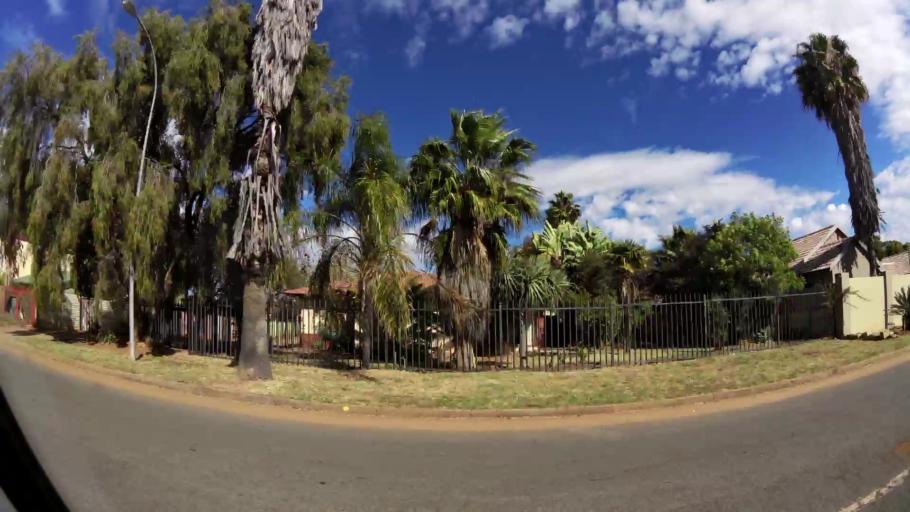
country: ZA
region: Limpopo
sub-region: Waterberg District Municipality
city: Bela-Bela
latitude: -24.8808
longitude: 28.2958
